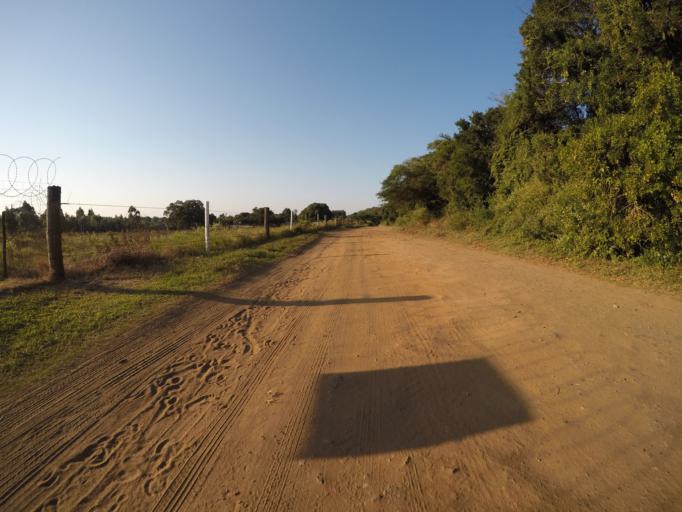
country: ZA
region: KwaZulu-Natal
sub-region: uThungulu District Municipality
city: KwaMbonambi
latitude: -28.7054
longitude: 32.1870
